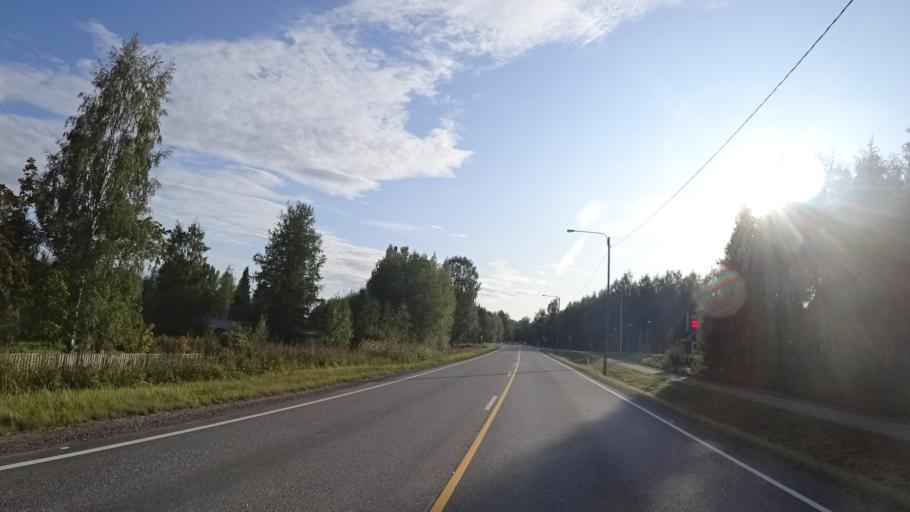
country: FI
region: South Karelia
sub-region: Imatra
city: Parikkala
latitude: 61.6075
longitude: 29.4937
